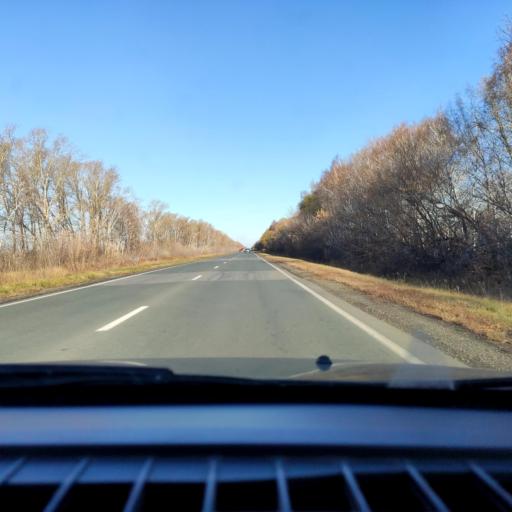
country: RU
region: Samara
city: Tol'yatti
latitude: 53.5990
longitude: 49.3238
